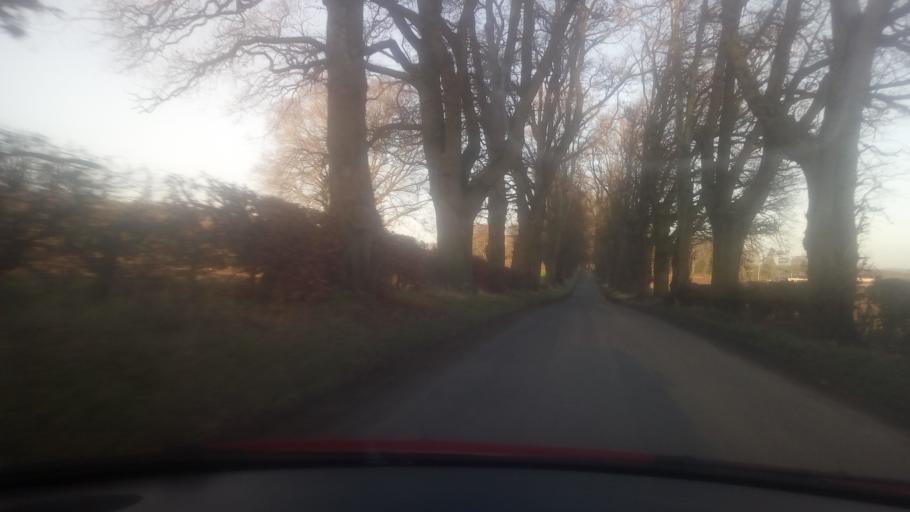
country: GB
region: Scotland
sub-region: The Scottish Borders
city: Jedburgh
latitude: 55.5225
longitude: -2.5272
